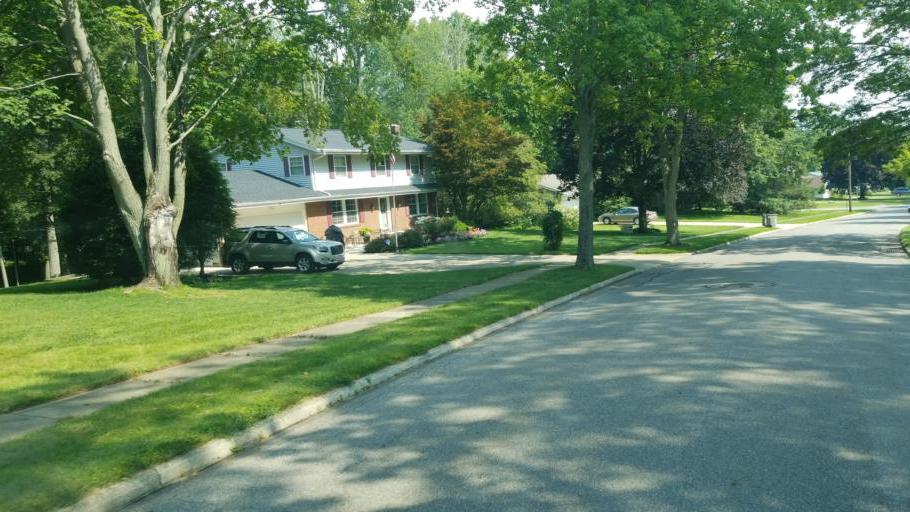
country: US
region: Ohio
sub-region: Richland County
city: Lexington
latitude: 40.6812
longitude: -82.6011
